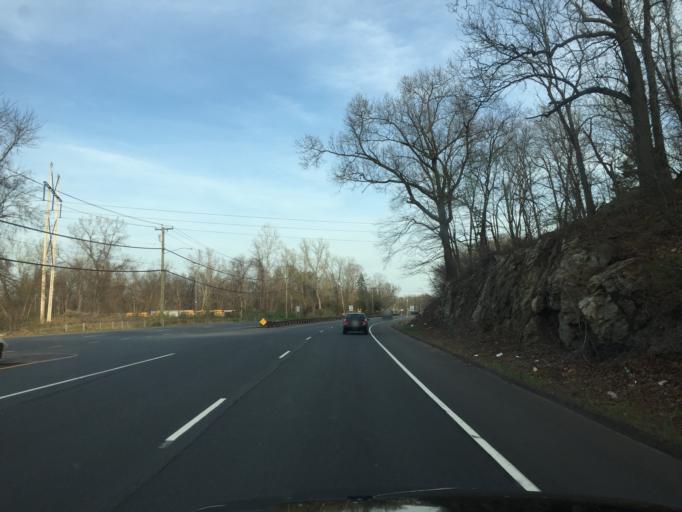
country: US
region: Connecticut
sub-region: Middlesex County
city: Portland
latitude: 41.5745
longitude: -72.6031
